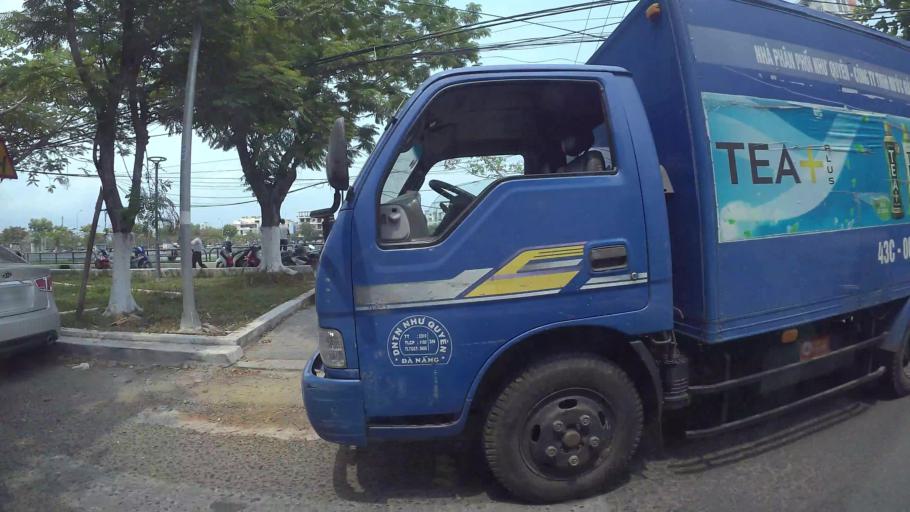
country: VN
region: Da Nang
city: Da Nang
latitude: 16.0625
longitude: 108.2116
